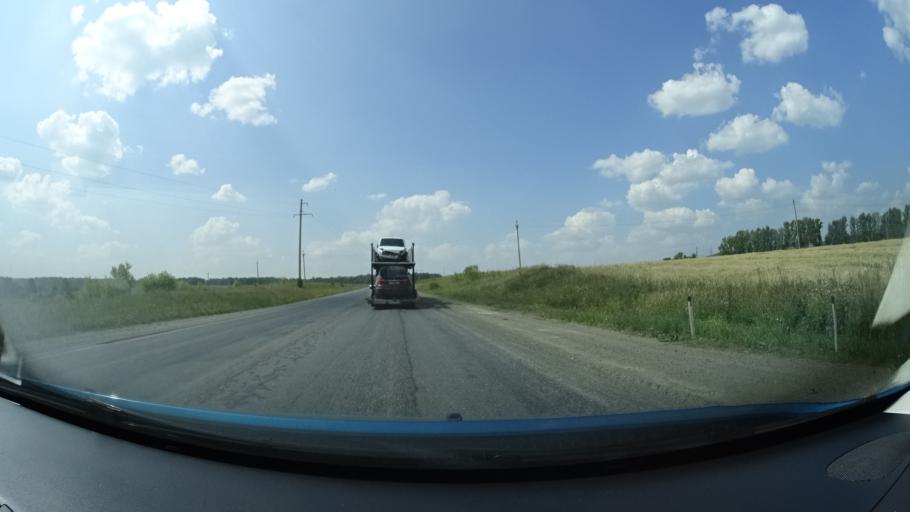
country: RU
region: Bashkortostan
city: Nizhnetroitskiy
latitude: 54.4548
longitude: 53.6616
